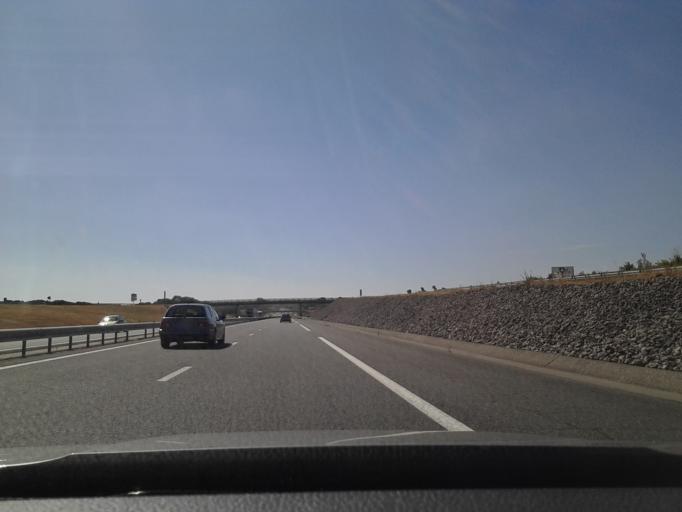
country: FR
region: Midi-Pyrenees
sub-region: Departement de l'Aveyron
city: La Cavalerie
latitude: 44.0136
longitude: 3.1385
